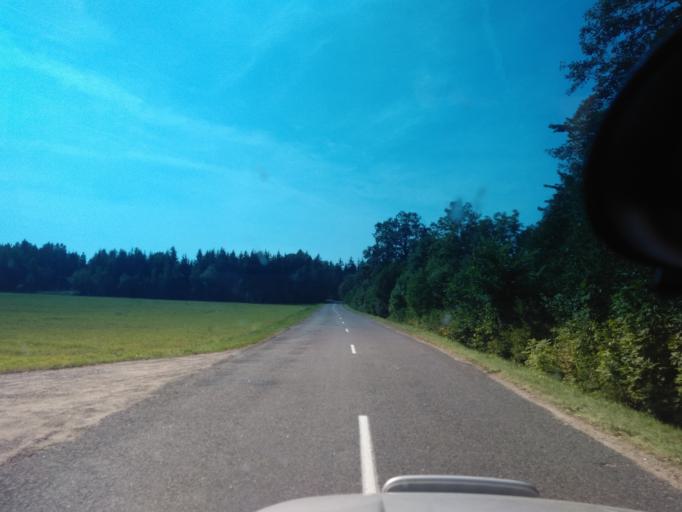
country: BY
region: Minsk
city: Kapyl'
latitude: 53.1857
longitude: 27.1116
